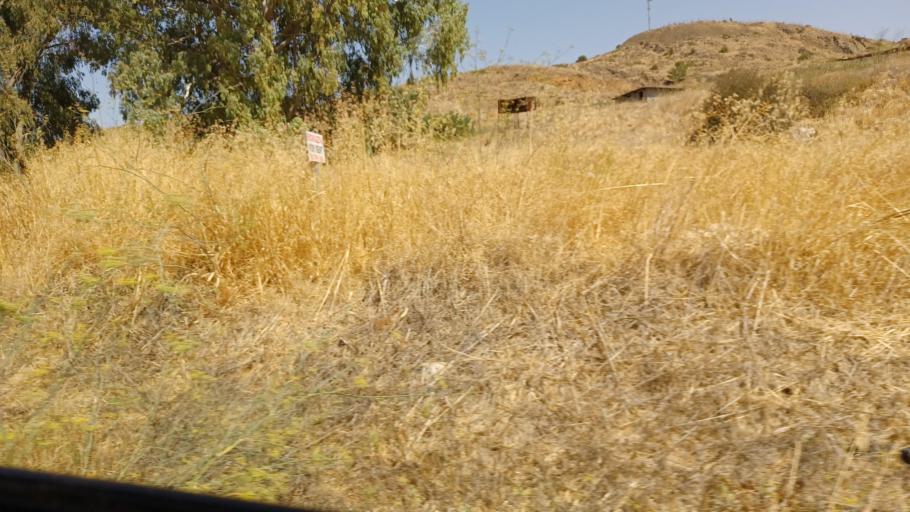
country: CY
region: Lefkosia
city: Lefka
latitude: 35.0655
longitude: 32.8959
